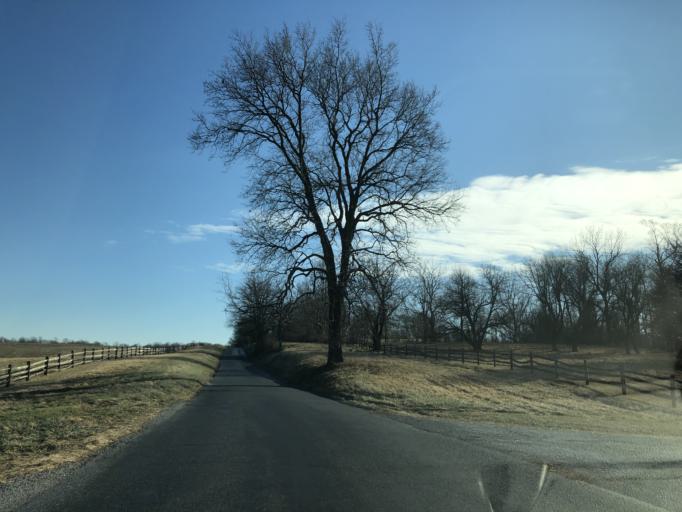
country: US
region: Pennsylvania
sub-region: Chester County
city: Upland
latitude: 39.8973
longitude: -75.7816
